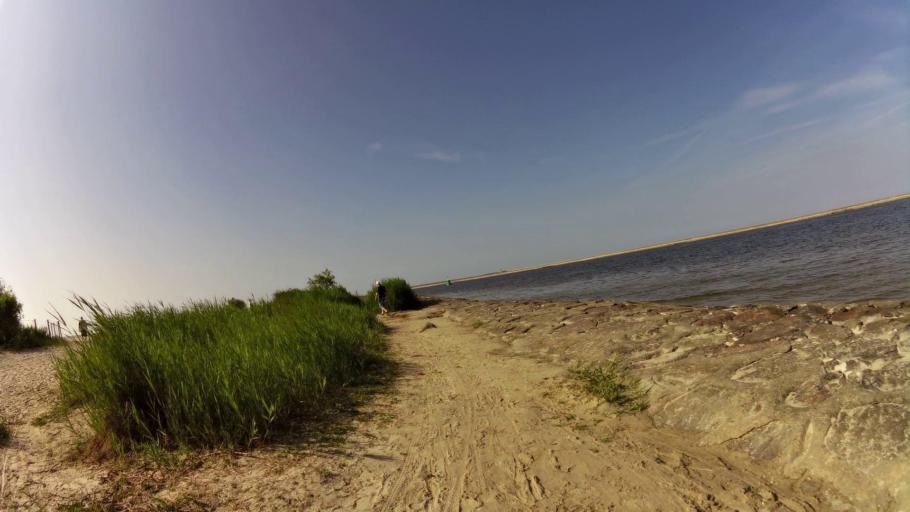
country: PL
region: West Pomeranian Voivodeship
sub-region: Swinoujscie
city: Swinoujscie
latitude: 53.9230
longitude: 14.2793
